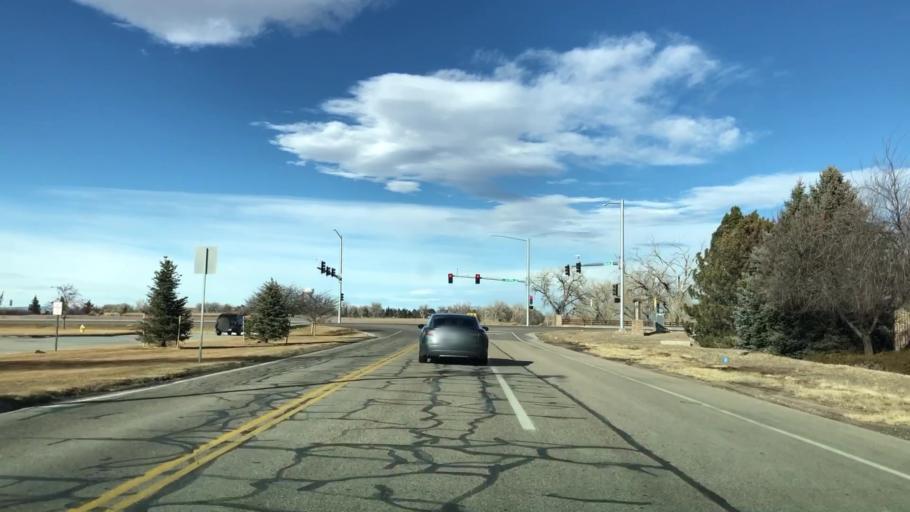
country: US
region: Colorado
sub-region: Weld County
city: Windsor
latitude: 40.5221
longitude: -104.9633
